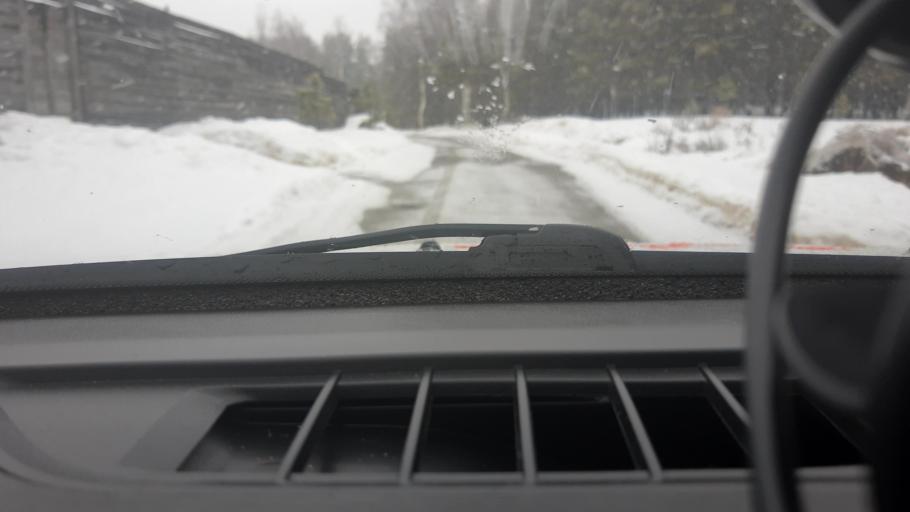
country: RU
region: Nizjnij Novgorod
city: Gorbatovka
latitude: 56.3279
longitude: 43.7753
